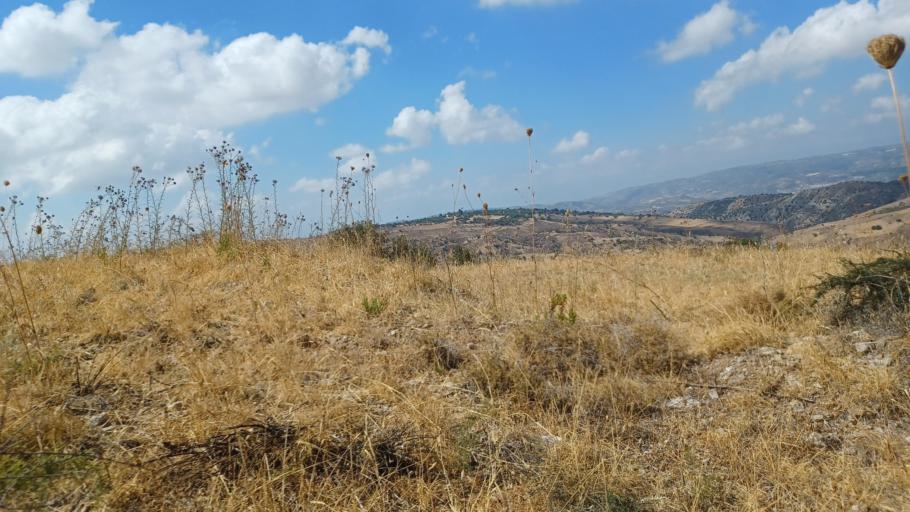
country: CY
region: Pafos
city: Mesogi
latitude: 34.8751
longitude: 32.5995
